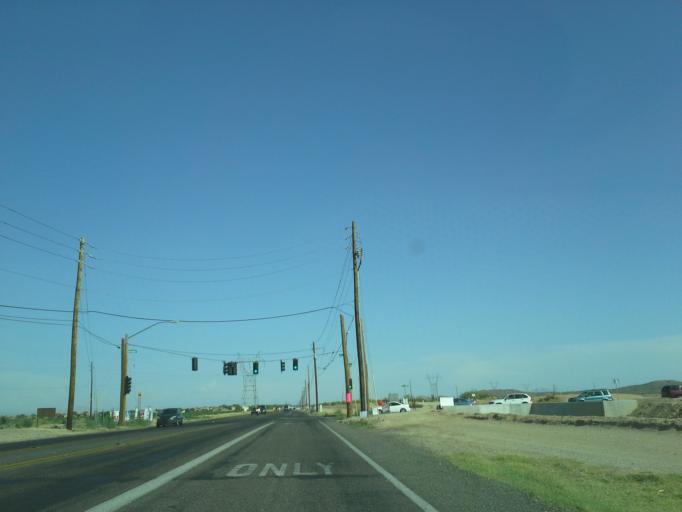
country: US
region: Arizona
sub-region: Pinal County
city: San Tan Valley
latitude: 33.1470
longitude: -111.5506
